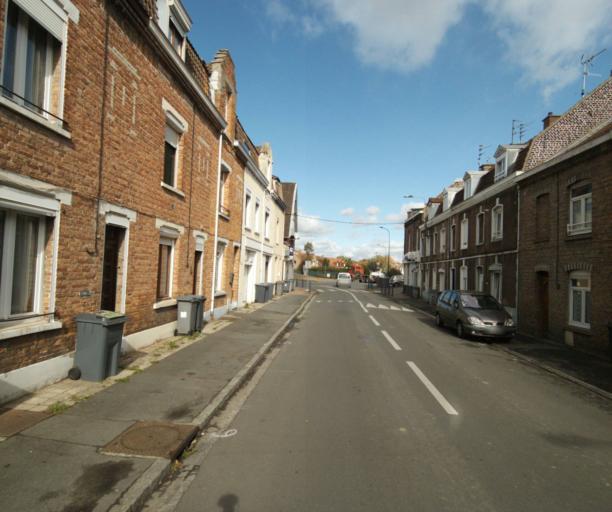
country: FR
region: Nord-Pas-de-Calais
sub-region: Departement du Nord
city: Armentieres
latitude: 50.6761
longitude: 2.8885
